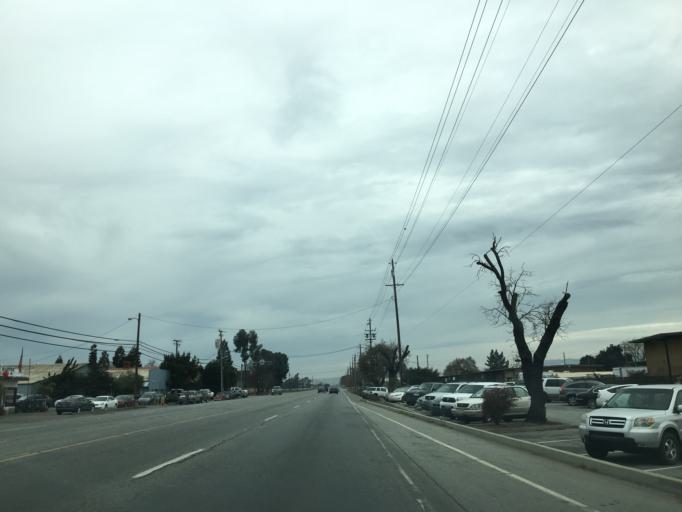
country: US
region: California
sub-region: Santa Clara County
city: San Martin
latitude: 37.0861
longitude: -121.6109
